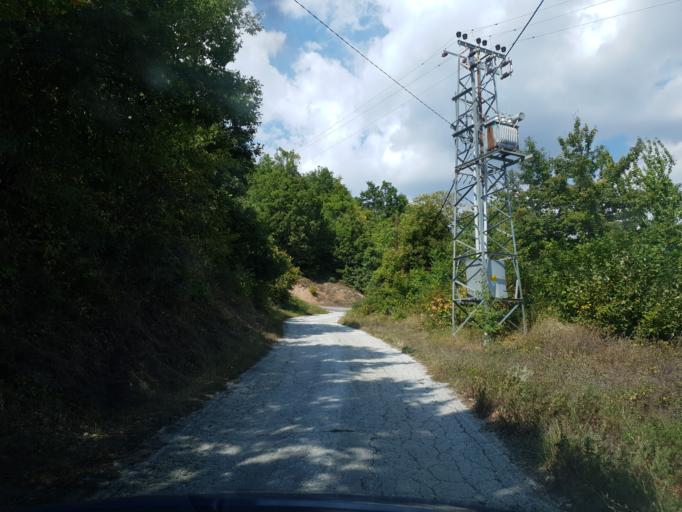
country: MK
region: Makedonski Brod
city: Samokov
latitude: 41.7447
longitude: 21.1052
